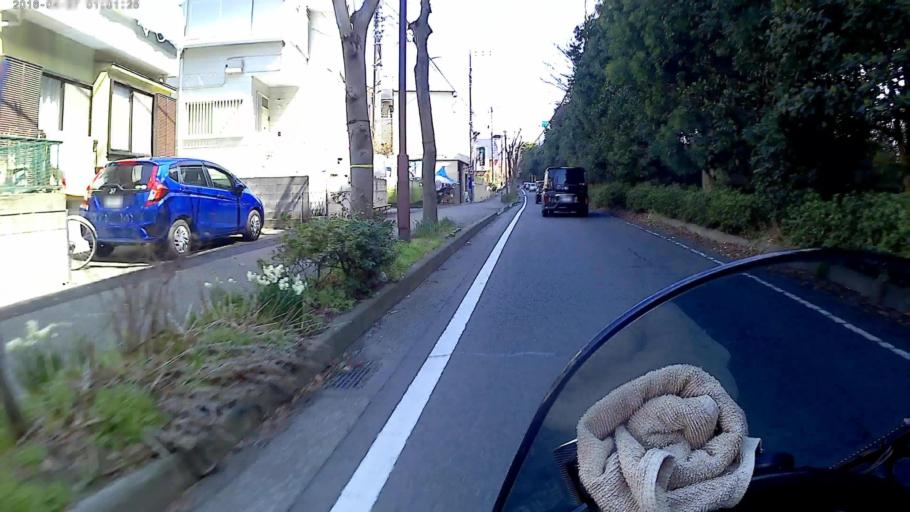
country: JP
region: Kanagawa
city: Chigasaki
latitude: 35.3475
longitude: 139.4248
